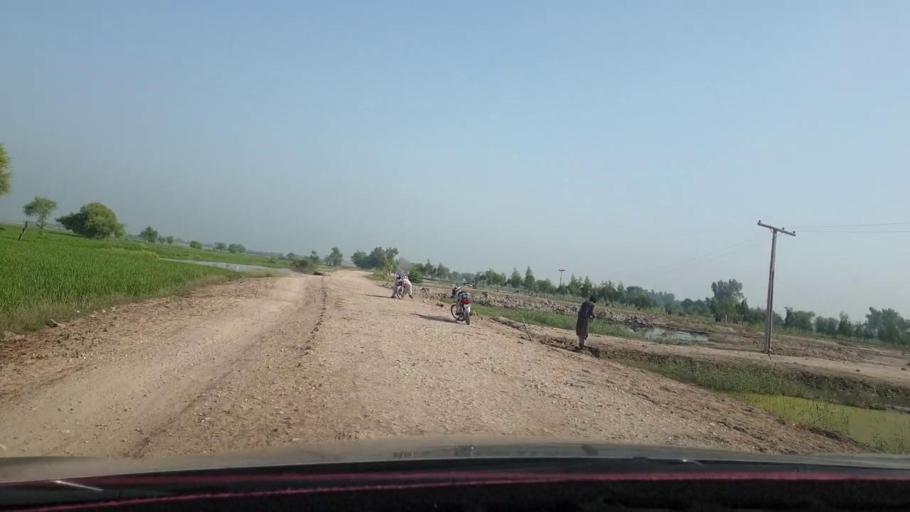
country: PK
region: Sindh
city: Nasirabad
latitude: 27.4548
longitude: 67.9176
